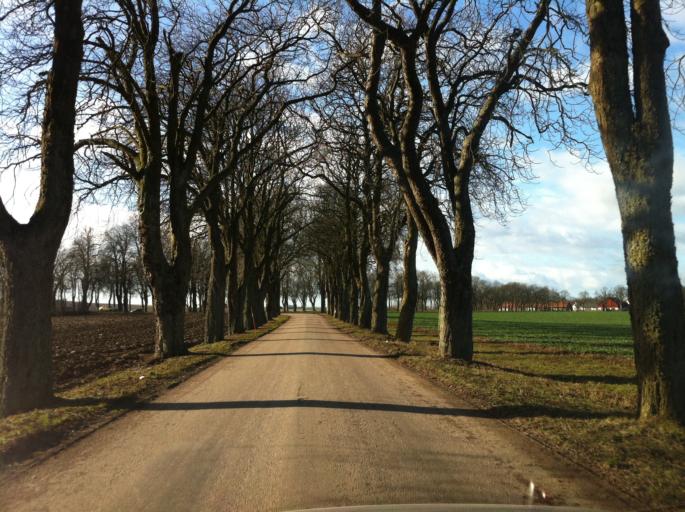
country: SE
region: Skane
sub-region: Landskrona
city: Asmundtorp
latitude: 55.9549
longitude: 12.9462
